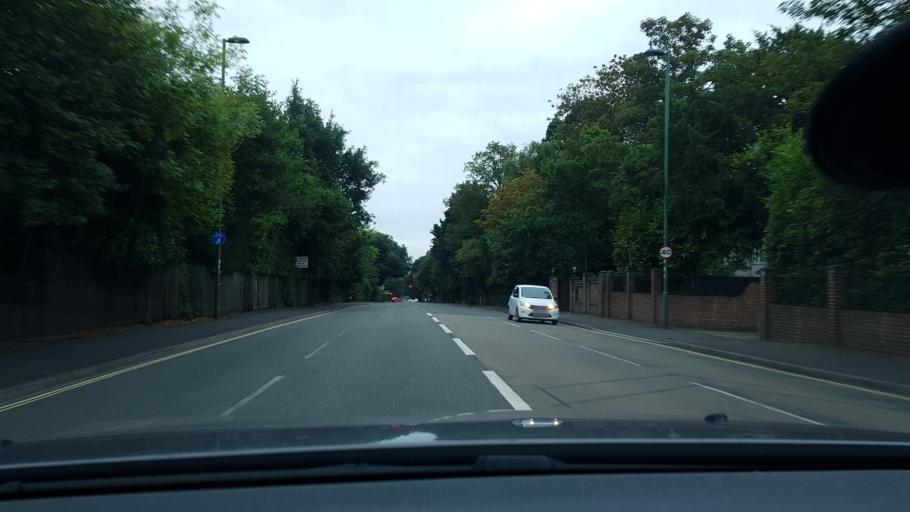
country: GB
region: England
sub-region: Southampton
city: Southampton
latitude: 50.9390
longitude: -1.4067
